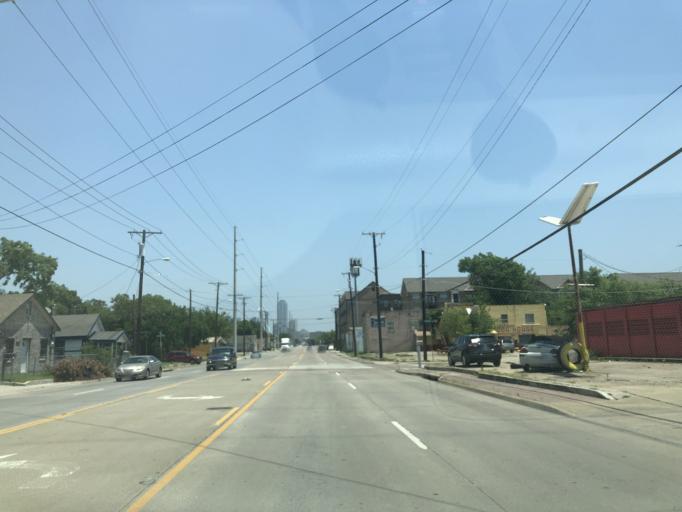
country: US
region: Texas
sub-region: Dallas County
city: Dallas
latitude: 32.7785
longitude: -96.8437
